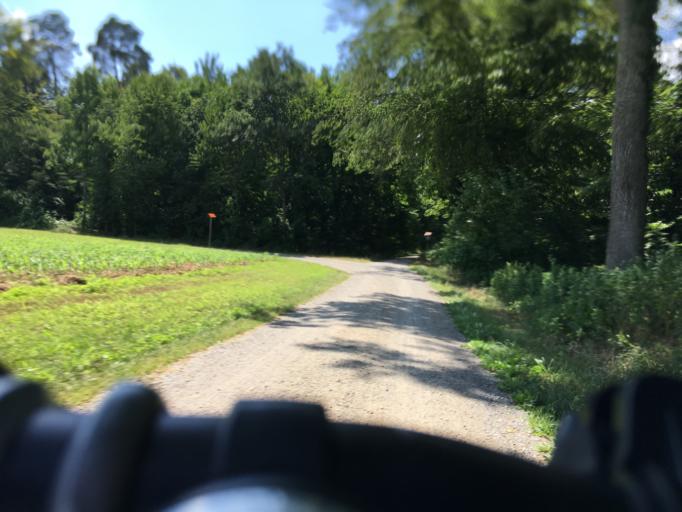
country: CH
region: Thurgau
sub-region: Frauenfeld District
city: Diessenhofen
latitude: 47.6886
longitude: 8.7183
